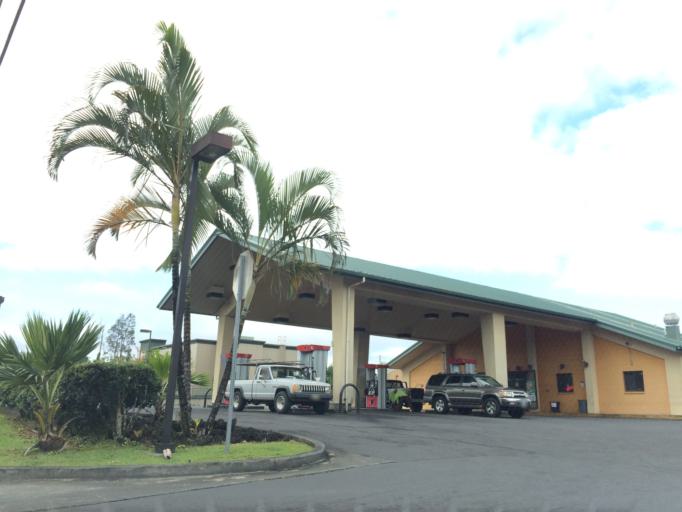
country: US
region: Hawaii
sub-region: Hawaii County
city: Hawaiian Paradise Park
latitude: 19.5041
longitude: -154.9544
